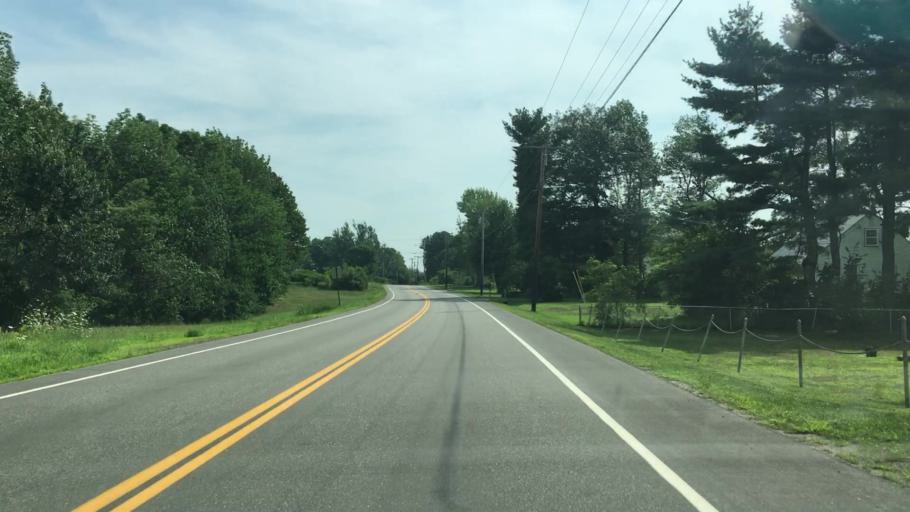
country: US
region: Maine
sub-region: Kennebec County
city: Windsor
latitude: 44.2965
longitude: -69.5849
